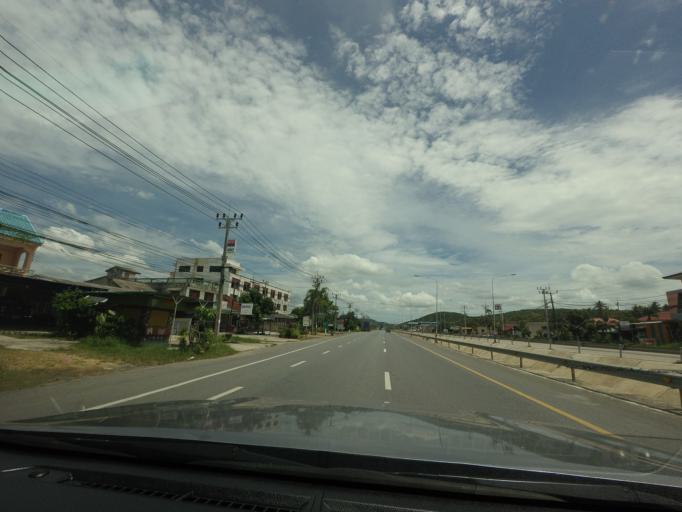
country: TH
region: Songkhla
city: Ban Mai
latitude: 7.2084
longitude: 100.5560
